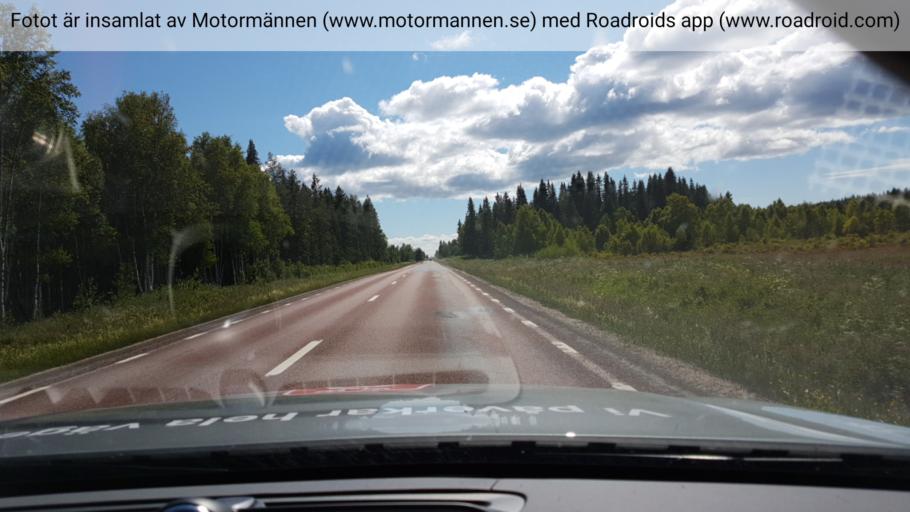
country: SE
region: Jaemtland
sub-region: Stroemsunds Kommun
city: Stroemsund
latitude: 63.7901
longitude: 15.5126
